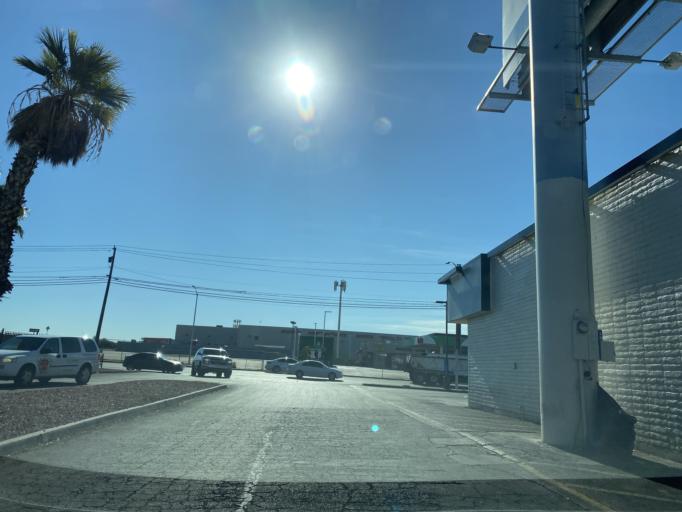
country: US
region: Nevada
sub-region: Clark County
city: Spring Valley
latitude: 36.1014
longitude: -115.2069
